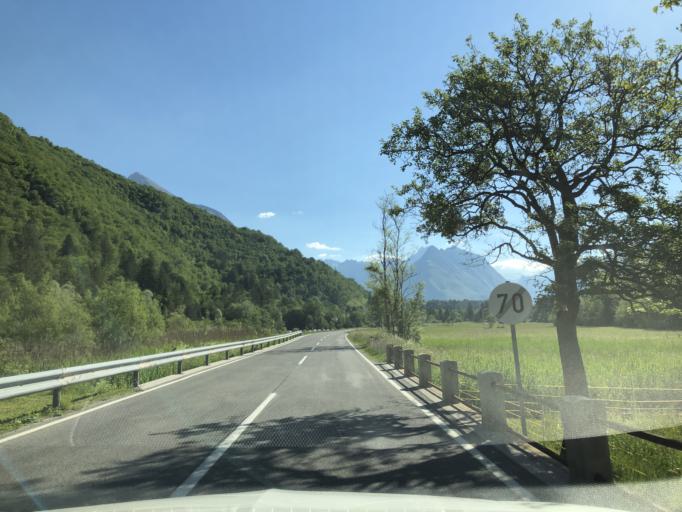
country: SI
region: Bovec
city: Bovec
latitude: 46.3202
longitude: 13.5002
